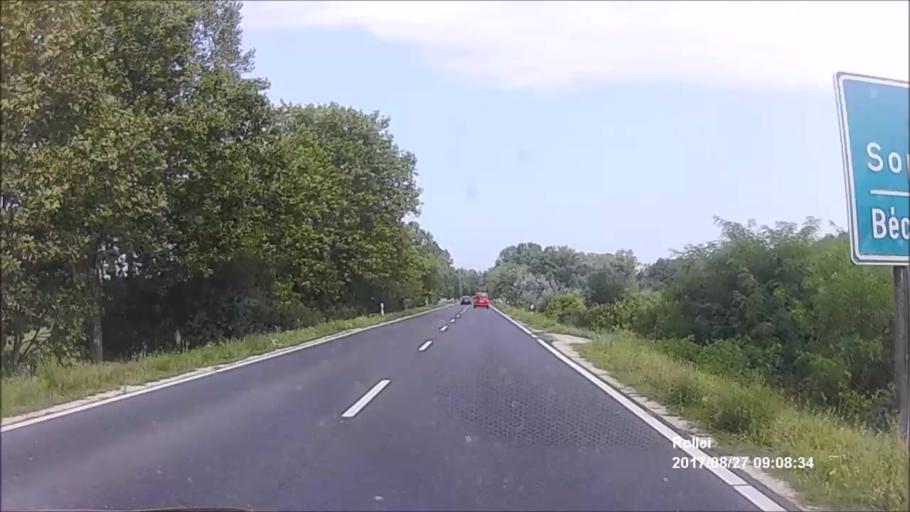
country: HU
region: Vas
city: Sarvar
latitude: 47.3639
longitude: 16.8938
